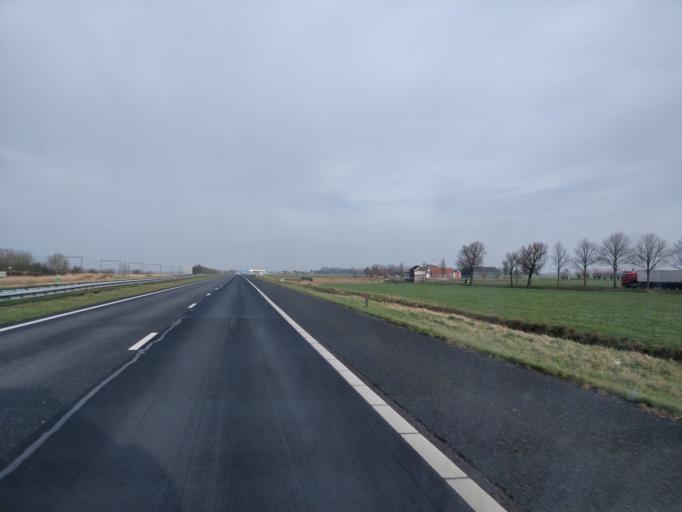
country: NL
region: Friesland
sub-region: Gemeente Boarnsterhim
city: Reduzum
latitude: 53.1216
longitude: 5.8082
